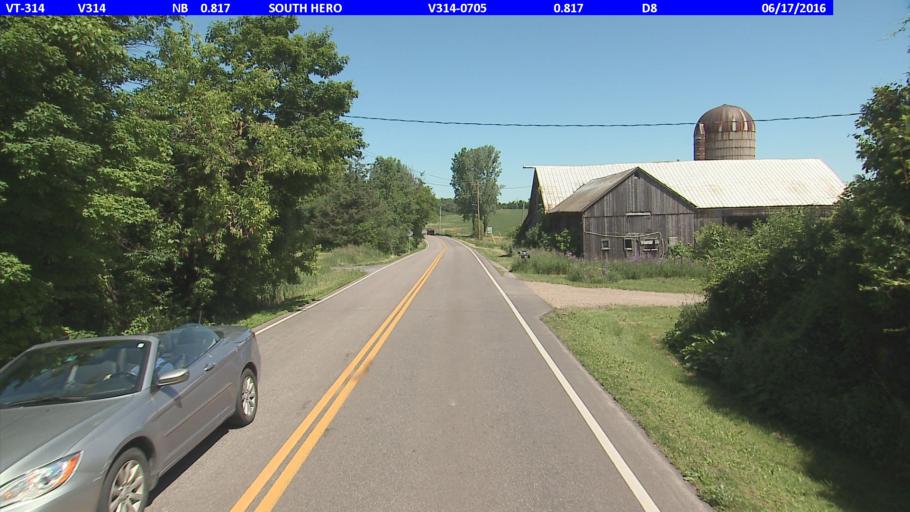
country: US
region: New York
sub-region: Clinton County
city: Cumberland Head
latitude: 44.6701
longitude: -73.3364
